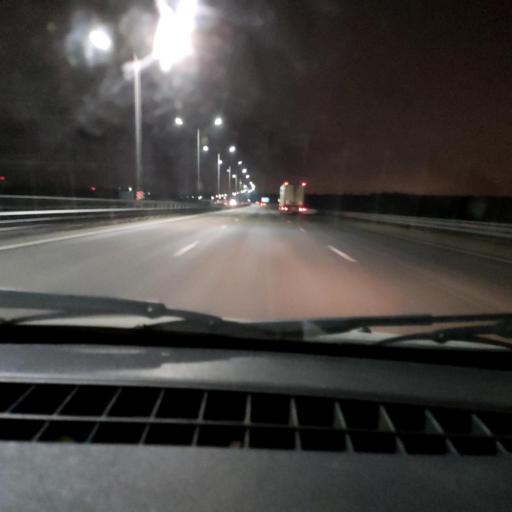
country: RU
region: Voronezj
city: Somovo
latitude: 51.7536
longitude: 39.3062
